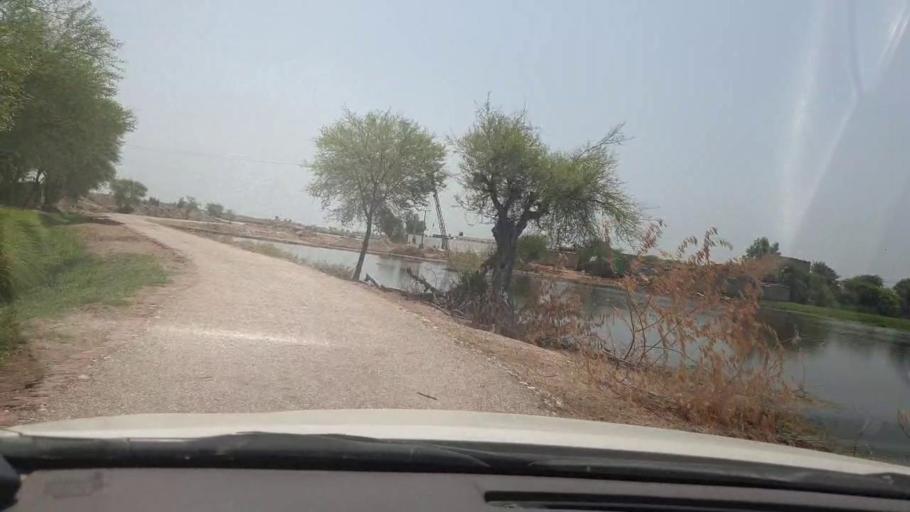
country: PK
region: Sindh
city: Garhi Yasin
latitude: 27.9089
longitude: 68.5536
